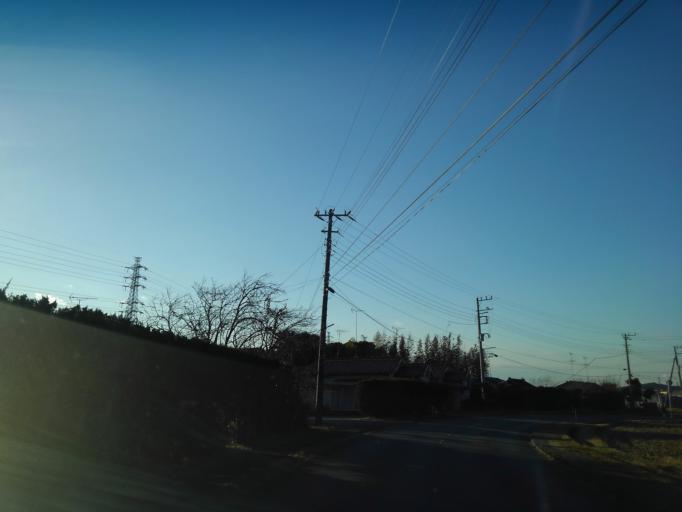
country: JP
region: Chiba
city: Kimitsu
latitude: 35.3218
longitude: 139.9058
